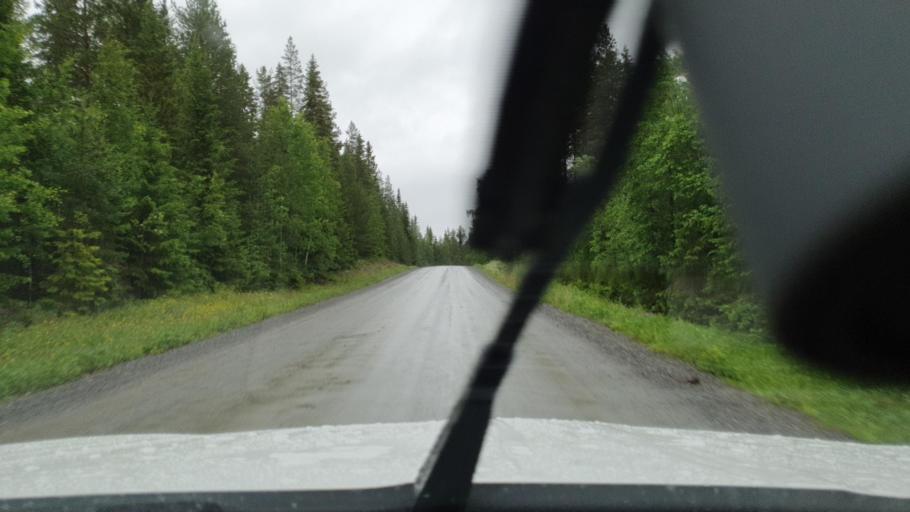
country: SE
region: Vaesterbotten
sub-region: Skelleftea Kommun
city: Burtraesk
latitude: 64.3681
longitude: 20.3954
